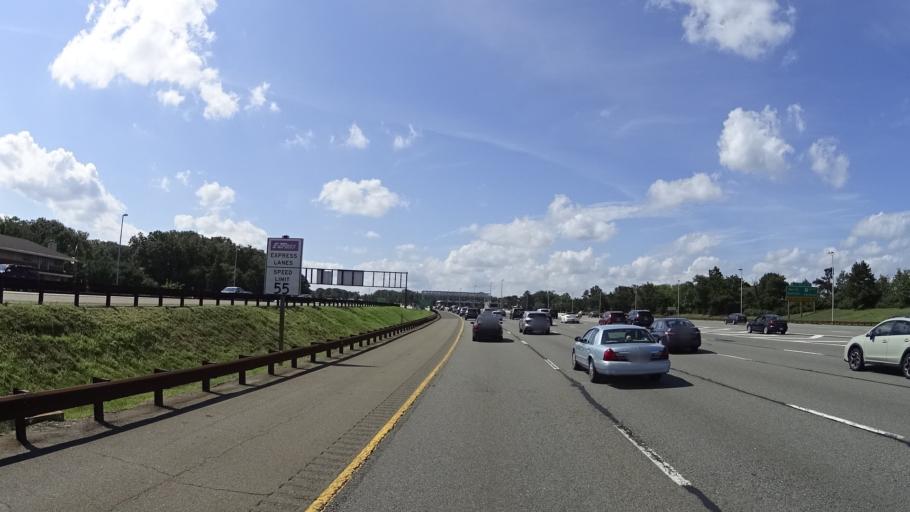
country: US
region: New Jersey
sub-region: Middlesex County
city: South Amboy
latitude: 40.4889
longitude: -74.3023
